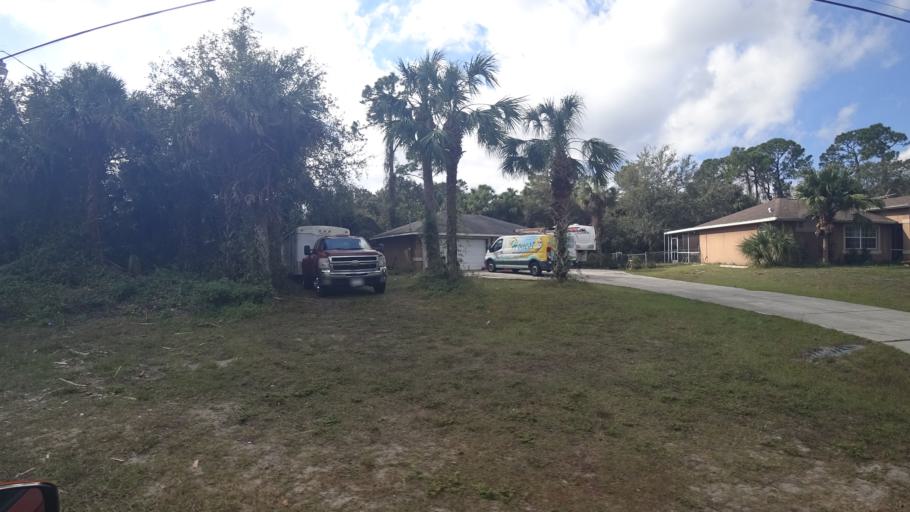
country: US
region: Florida
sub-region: Charlotte County
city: Port Charlotte
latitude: 27.0443
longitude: -82.1297
